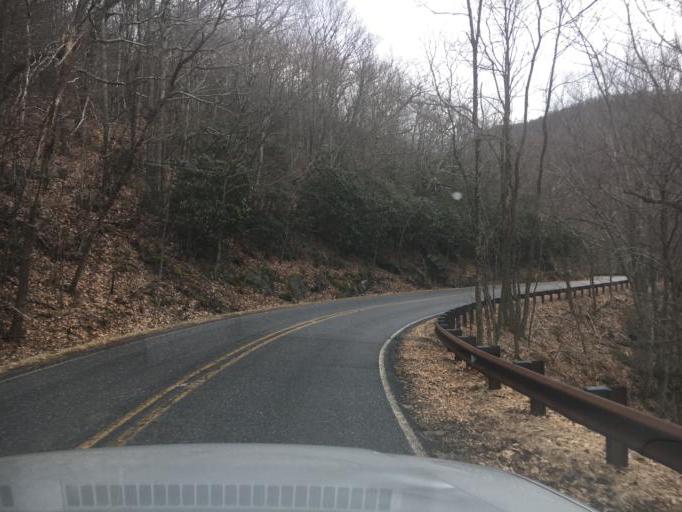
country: US
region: North Carolina
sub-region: Transylvania County
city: Brevard
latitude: 35.3699
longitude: -82.7929
